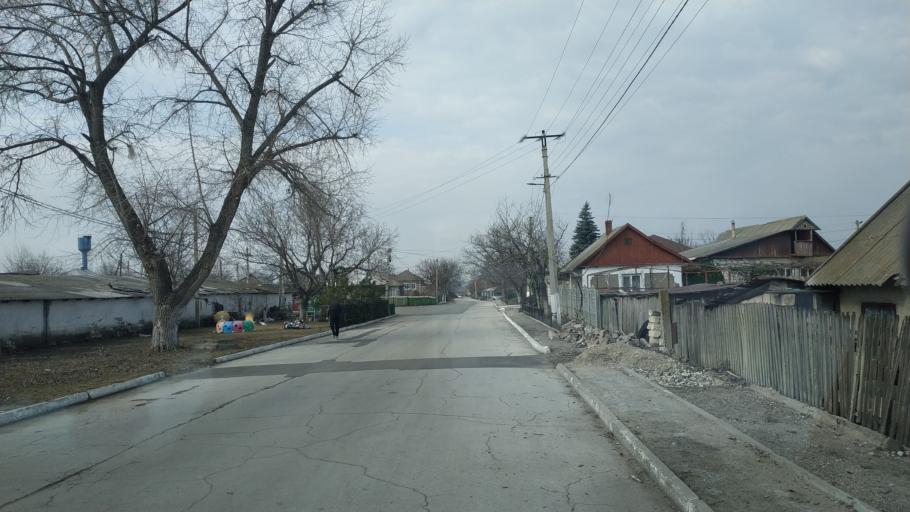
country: MD
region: Anenii Noi
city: Anenii Noi
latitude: 46.9024
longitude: 29.1326
